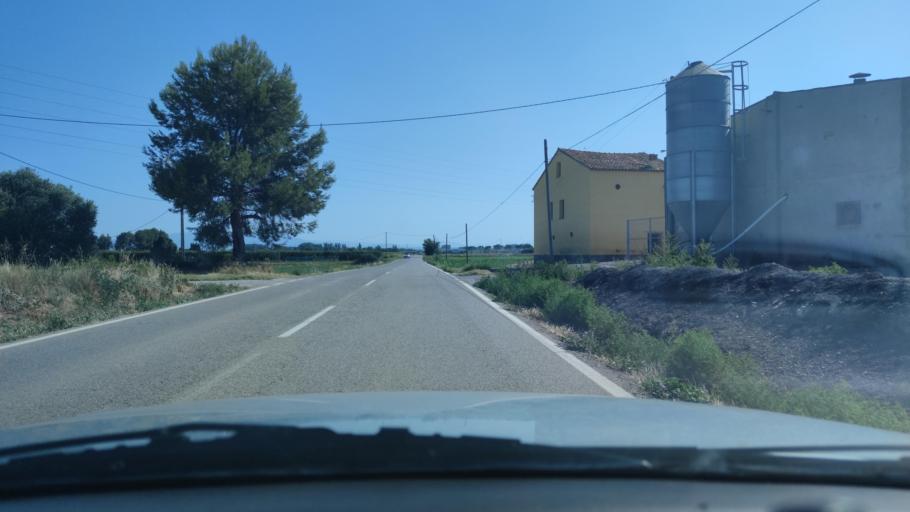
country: ES
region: Catalonia
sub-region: Provincia de Lleida
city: Bellvis
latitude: 41.6503
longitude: 0.8011
